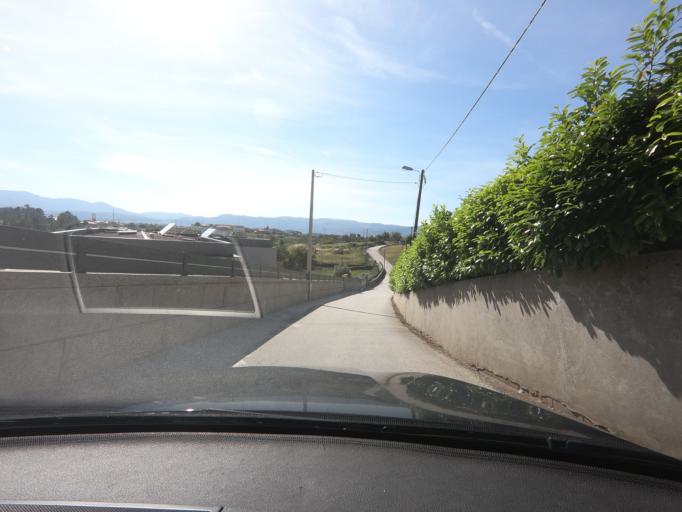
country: PT
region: Vila Real
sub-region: Vila Real
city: Vila Real
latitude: 41.2785
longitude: -7.6943
